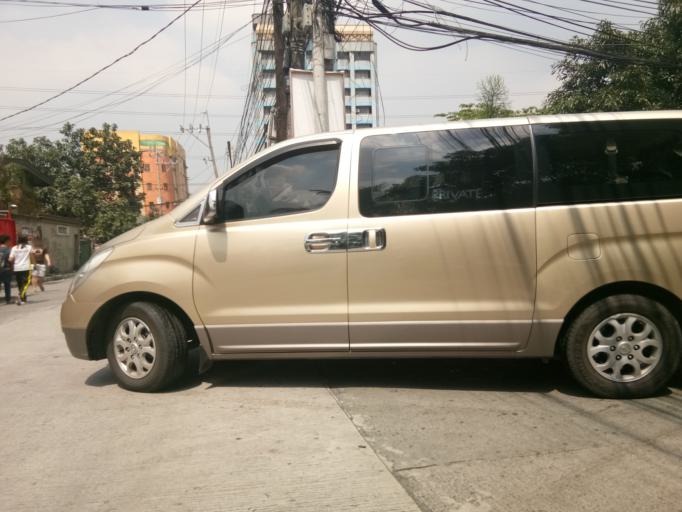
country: PH
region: Metro Manila
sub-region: Marikina
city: Calumpang
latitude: 14.6198
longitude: 121.0616
